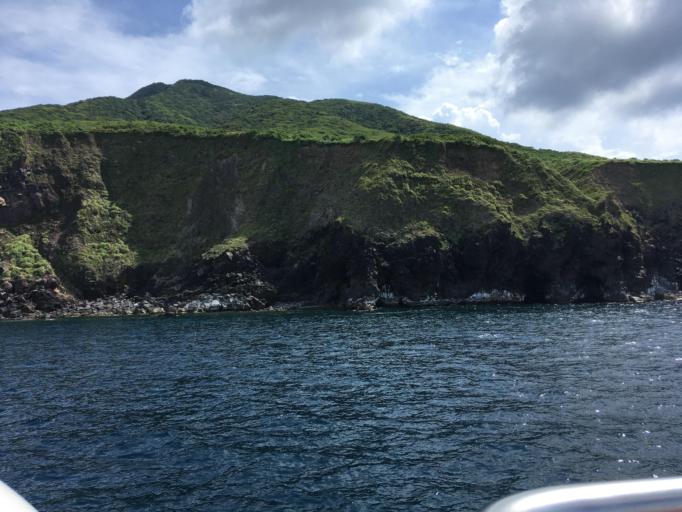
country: TW
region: Taiwan
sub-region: Yilan
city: Yilan
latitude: 24.8517
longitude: 121.9534
